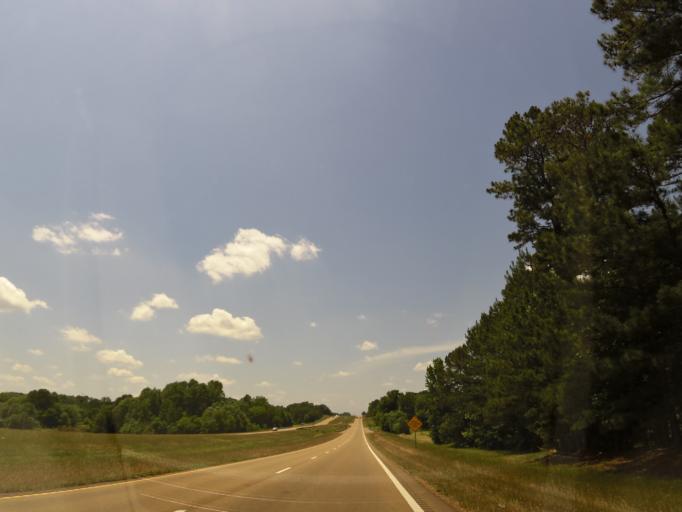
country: US
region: Mississippi
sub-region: Lafayette County
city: Oxford
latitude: 34.3031
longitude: -89.2654
